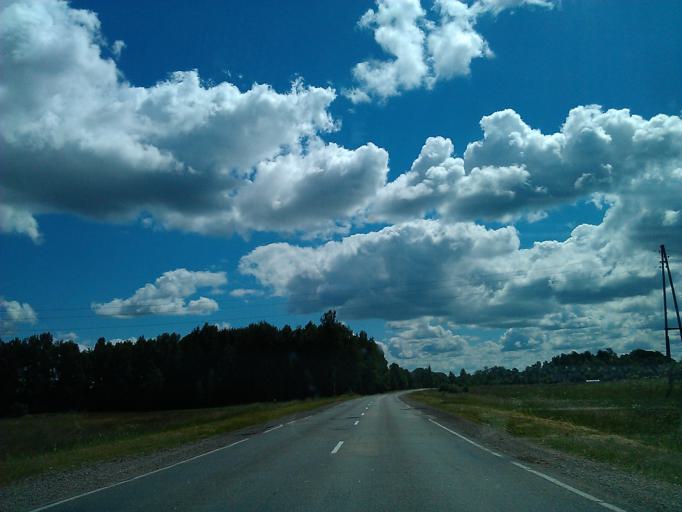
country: LV
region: Vilanu
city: Vilani
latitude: 56.5746
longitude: 26.9112
